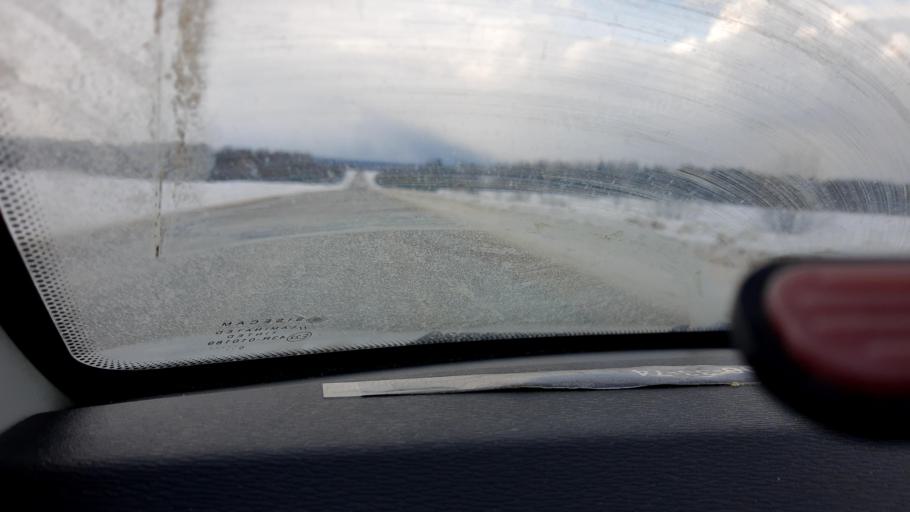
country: RU
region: Nizjnij Novgorod
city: Uren'
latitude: 57.4968
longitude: 45.8985
